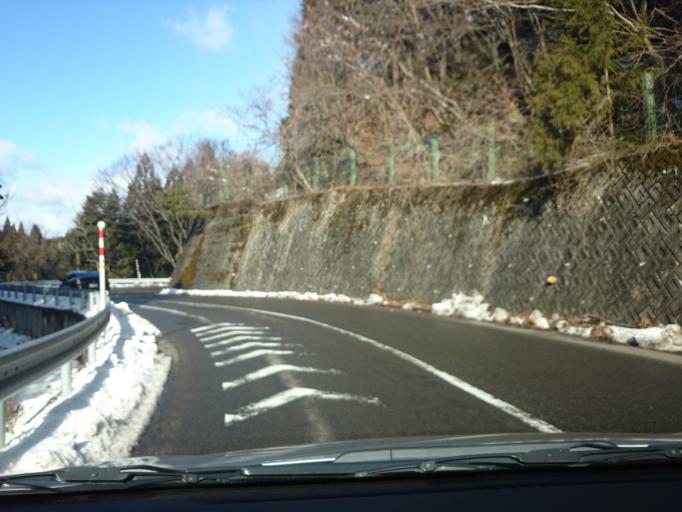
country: JP
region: Gifu
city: Gujo
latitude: 35.7386
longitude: 136.9862
